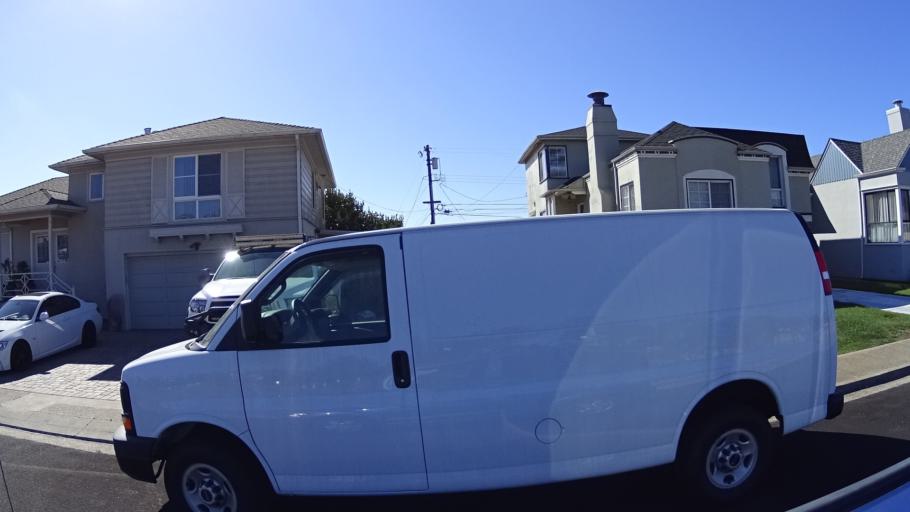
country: US
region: California
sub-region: San Mateo County
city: Broadmoor
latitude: 37.7042
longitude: -122.4798
